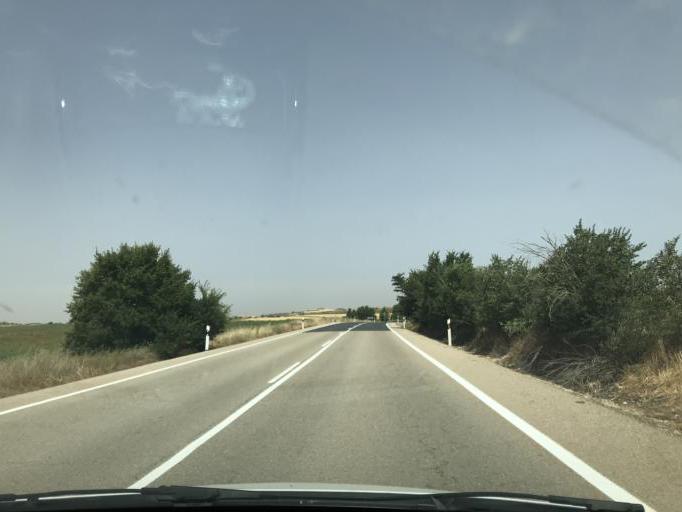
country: ES
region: Castille-La Mancha
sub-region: Provincia de Cuenca
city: Villar de Domingo Garcia
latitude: 40.2498
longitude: -2.3075
